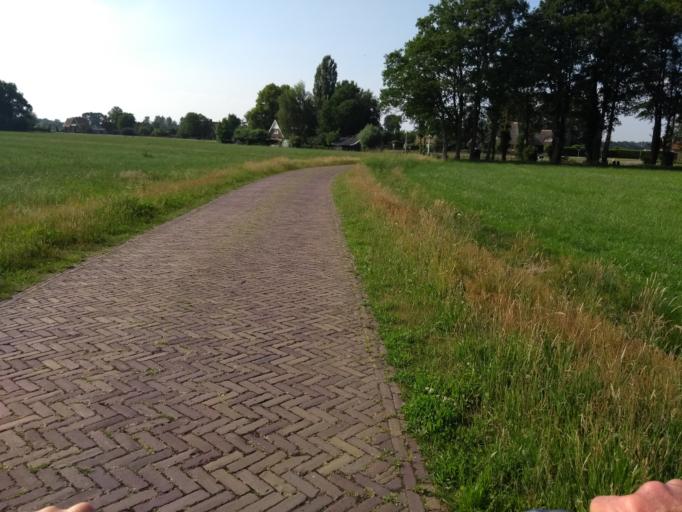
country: NL
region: Overijssel
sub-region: Gemeente Tubbergen
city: Tubbergen
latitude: 52.3702
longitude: 6.7472
